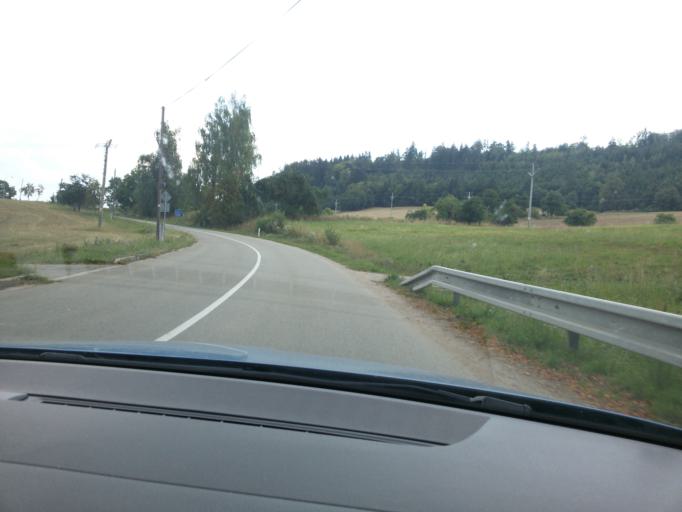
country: CZ
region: South Moravian
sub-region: Okres Brno-Venkov
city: Lomnice
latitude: 49.4120
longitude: 16.4073
